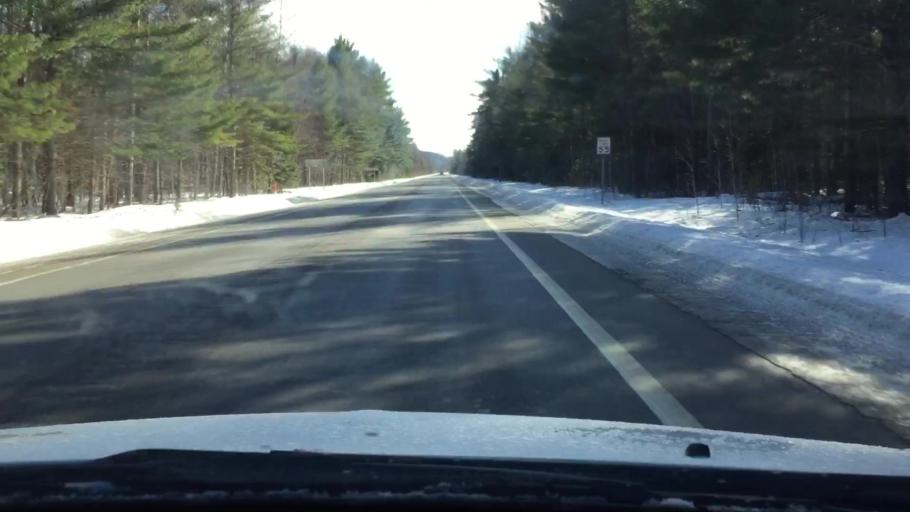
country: US
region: Michigan
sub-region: Antrim County
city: Mancelona
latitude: 45.0329
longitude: -85.0671
